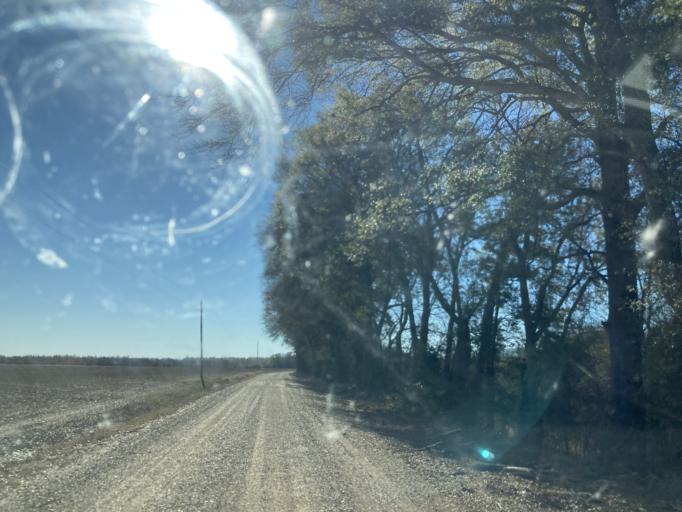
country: US
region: Mississippi
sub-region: Sharkey County
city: Rolling Fork
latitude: 32.7552
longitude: -90.6906
